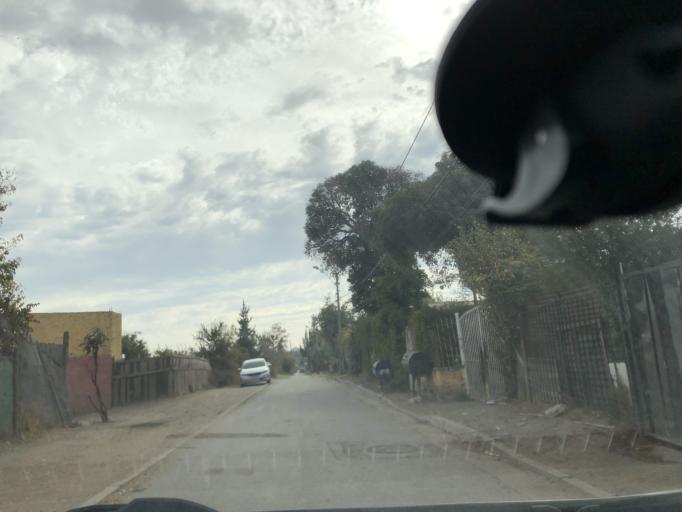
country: CL
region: Santiago Metropolitan
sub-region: Provincia de Cordillera
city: Puente Alto
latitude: -33.6118
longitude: -70.5367
